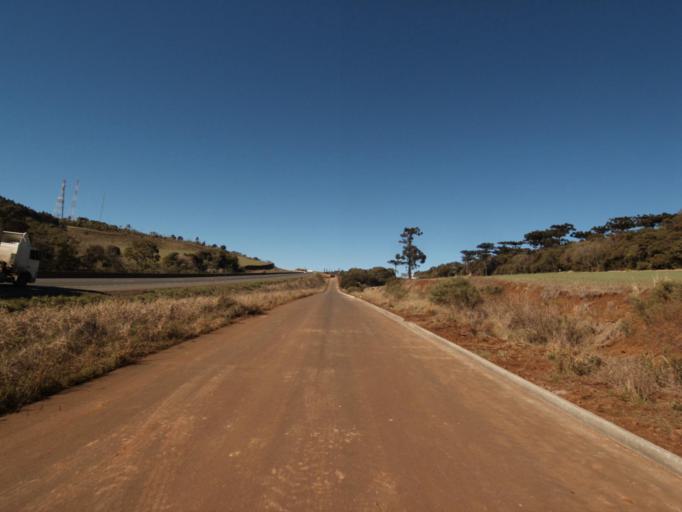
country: BR
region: Santa Catarina
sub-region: Xanxere
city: Xanxere
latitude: -26.8859
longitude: -52.4293
